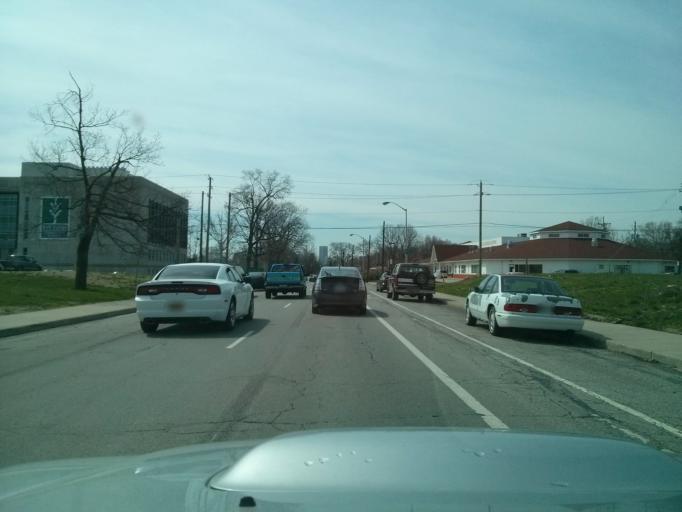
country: US
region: Indiana
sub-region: Marion County
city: Indianapolis
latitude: 39.8050
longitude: -86.1613
